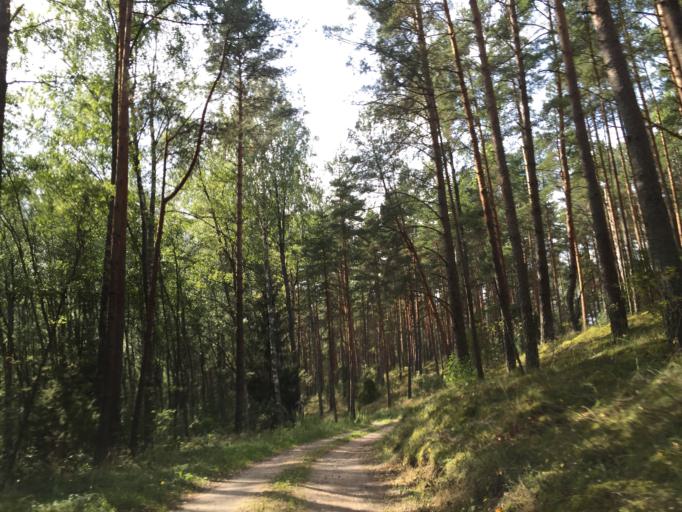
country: LV
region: Jurmala
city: Jurmala
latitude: 56.8705
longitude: 23.7063
